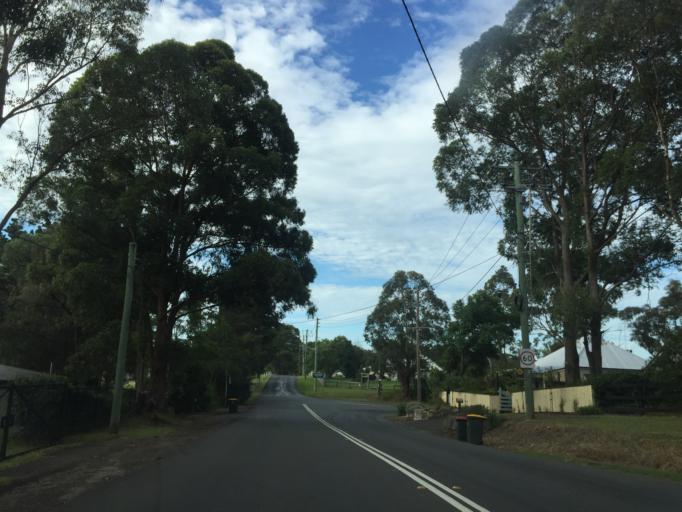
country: AU
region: New South Wales
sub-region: Hornsby Shire
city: Galston
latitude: -33.6525
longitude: 151.0573
